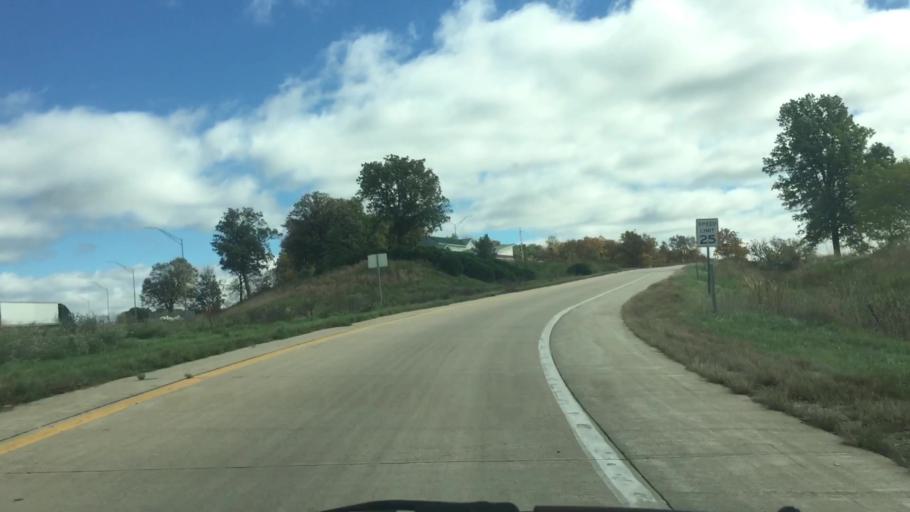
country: US
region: Iowa
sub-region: Poweshiek County
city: Grinnell
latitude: 41.6948
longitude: -92.7756
